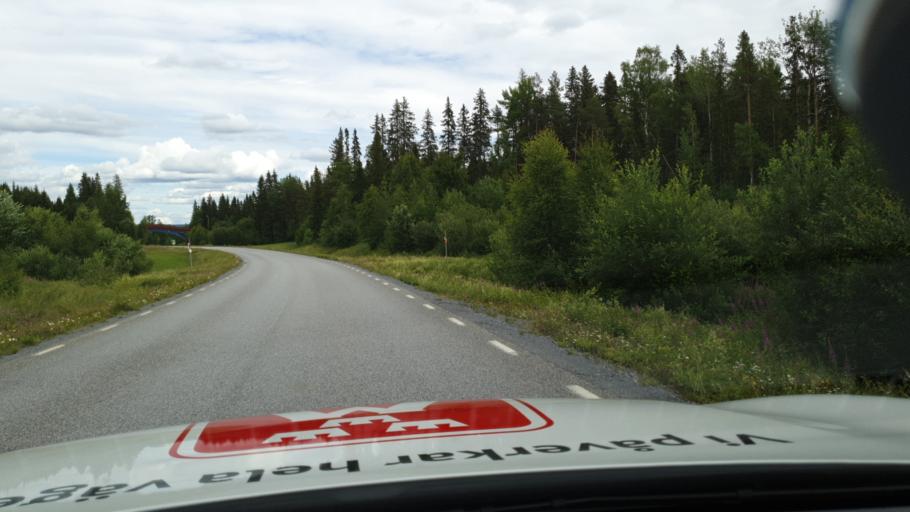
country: SE
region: Jaemtland
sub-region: OEstersunds Kommun
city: Lit
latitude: 63.3277
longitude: 14.8443
